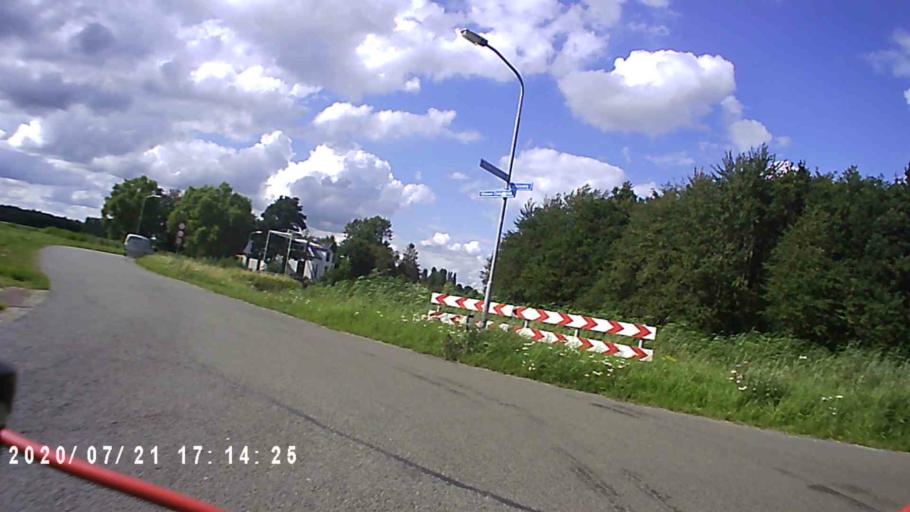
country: NL
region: Groningen
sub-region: Gemeente Hoogezand-Sappemeer
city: Hoogezand
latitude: 53.1415
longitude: 6.7573
